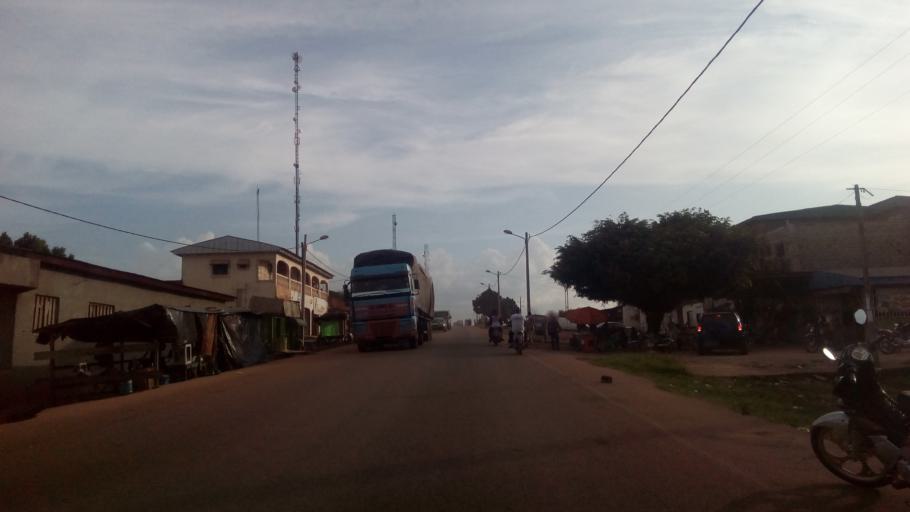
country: CI
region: Dix-Huit Montagnes
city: Duekoue
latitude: 6.7378
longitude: -7.3440
